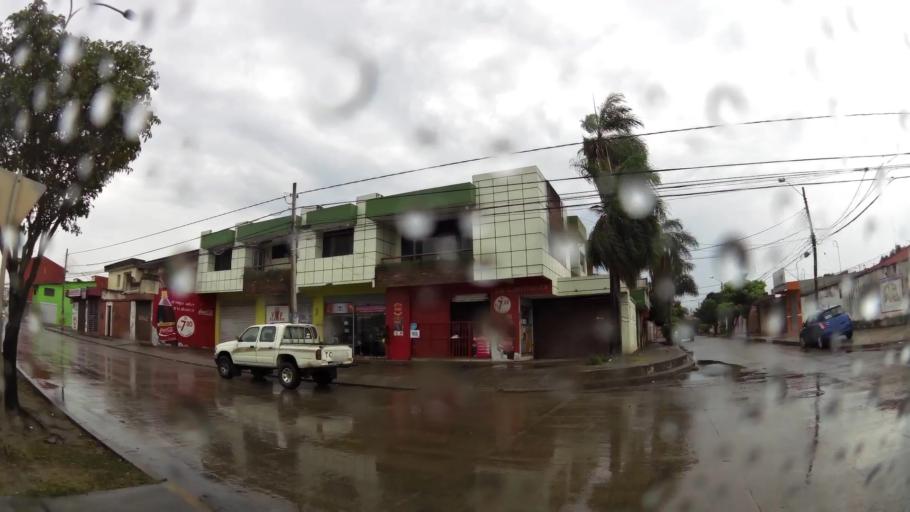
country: BO
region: Santa Cruz
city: Santa Cruz de la Sierra
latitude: -17.7665
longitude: -63.1508
